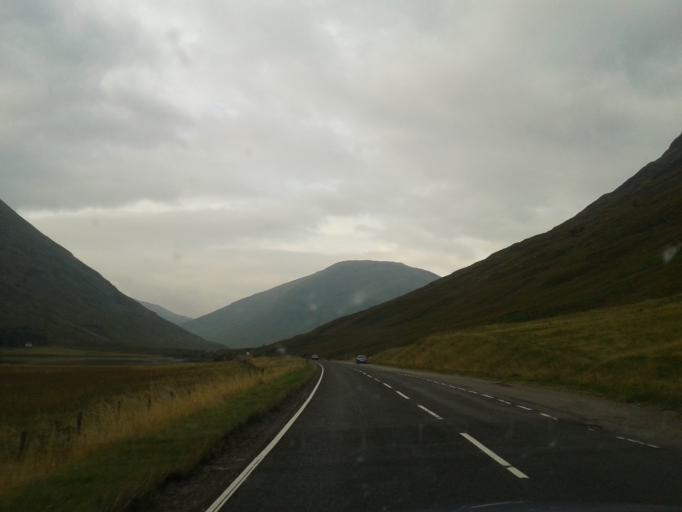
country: GB
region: Scotland
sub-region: Highland
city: Fort William
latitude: 56.6692
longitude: -5.0256
